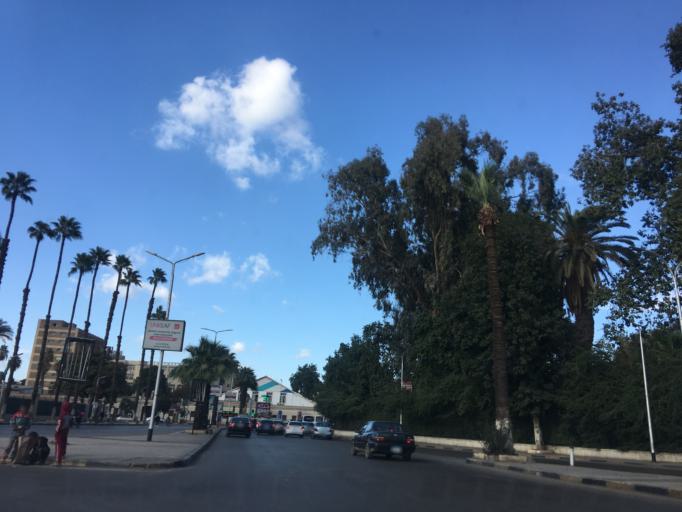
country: EG
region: Al Jizah
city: Al Jizah
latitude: 30.0285
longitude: 31.2106
